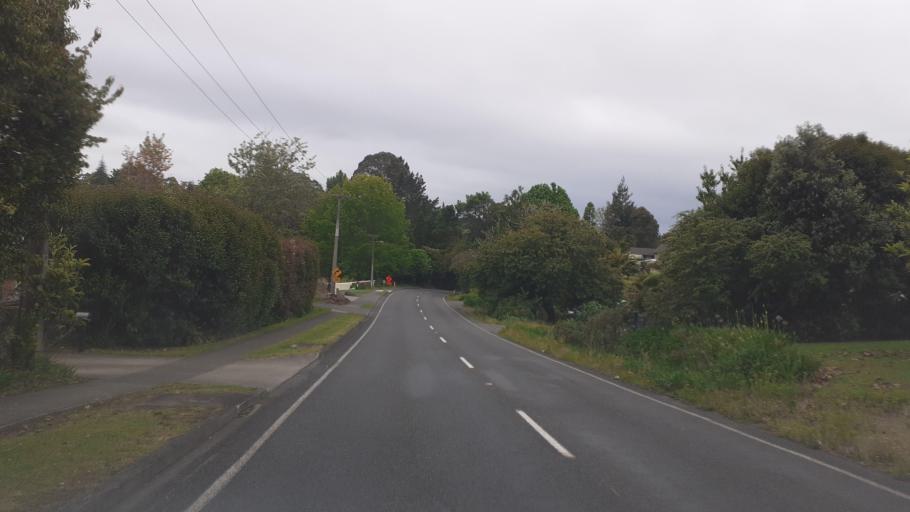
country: NZ
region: Northland
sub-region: Far North District
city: Kerikeri
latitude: -35.2051
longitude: 173.9661
